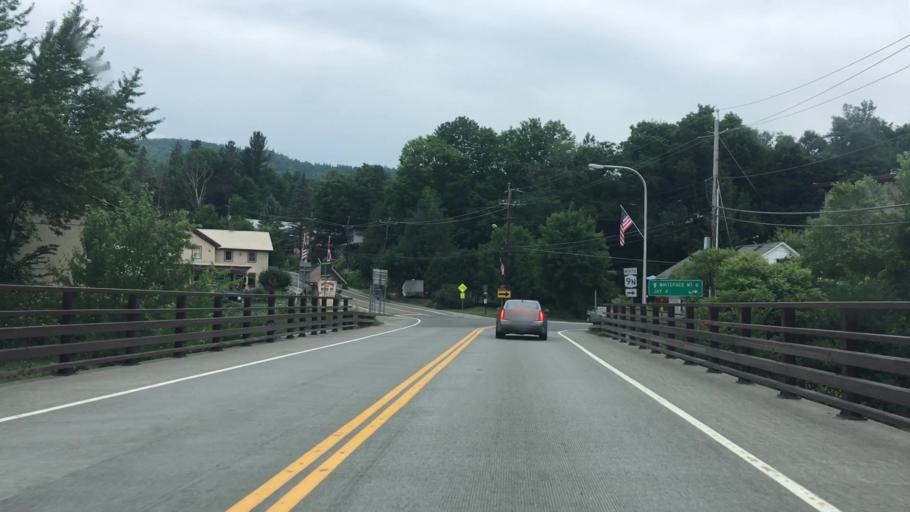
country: US
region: New York
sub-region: Essex County
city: Lake Placid
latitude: 44.3357
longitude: -73.7754
